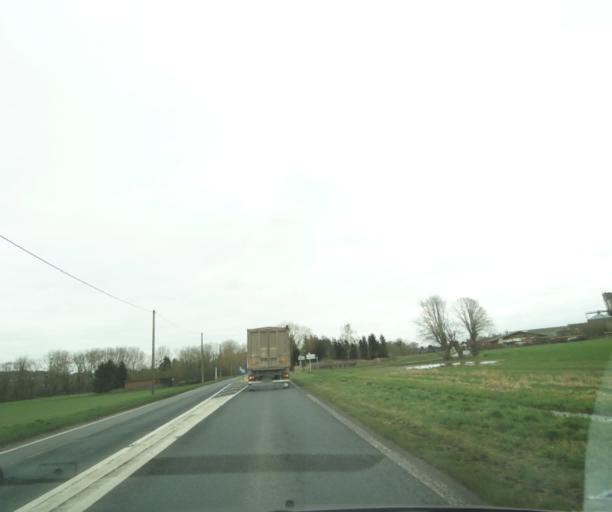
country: FR
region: Picardie
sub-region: Departement de l'Oise
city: Noyon
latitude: 49.5910
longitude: 2.9845
